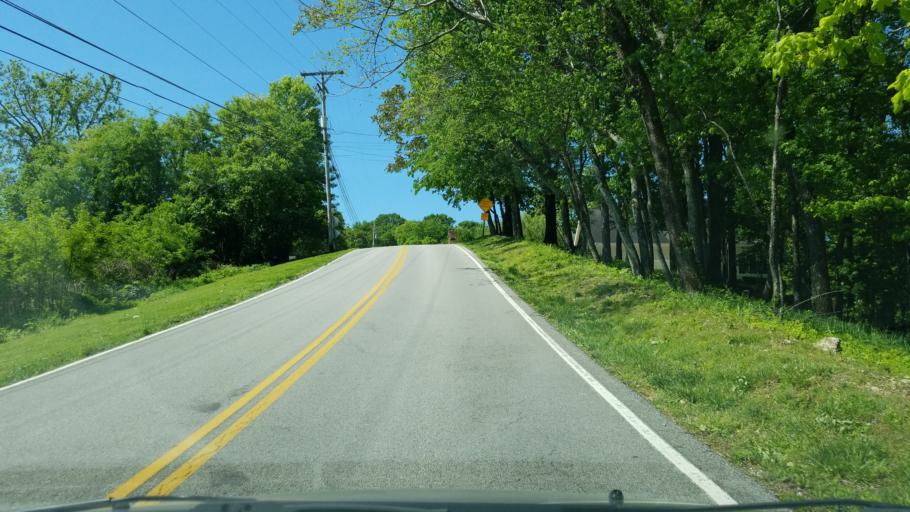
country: US
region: Tennessee
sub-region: Hamilton County
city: Middle Valley
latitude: 35.1626
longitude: -85.1843
